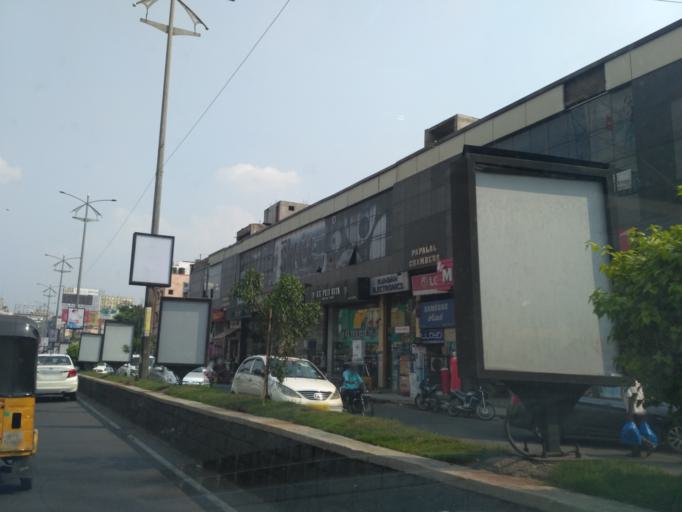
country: IN
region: Telangana
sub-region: Hyderabad
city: Hyderabad
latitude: 17.4040
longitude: 78.4818
